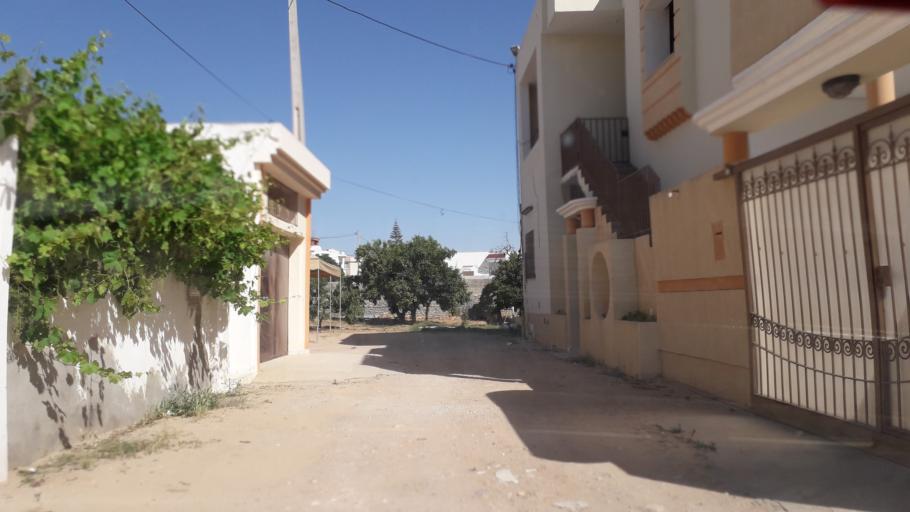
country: TN
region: Safaqis
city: Al Qarmadah
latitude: 34.8077
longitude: 10.7657
